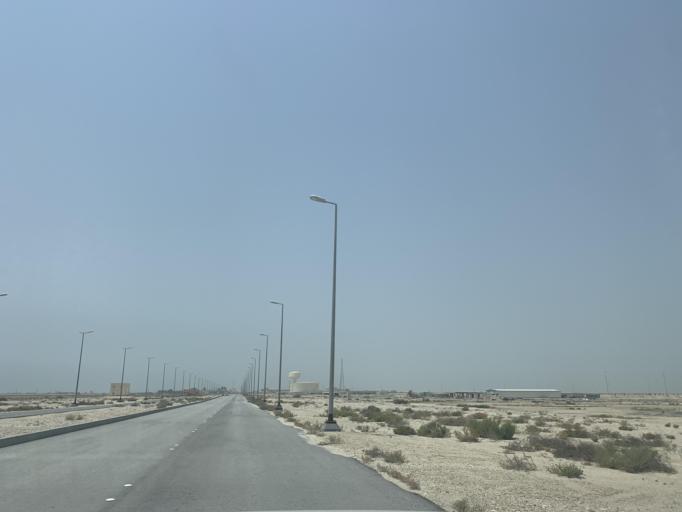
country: BH
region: Central Governorate
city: Dar Kulayb
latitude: 25.8469
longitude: 50.5910
